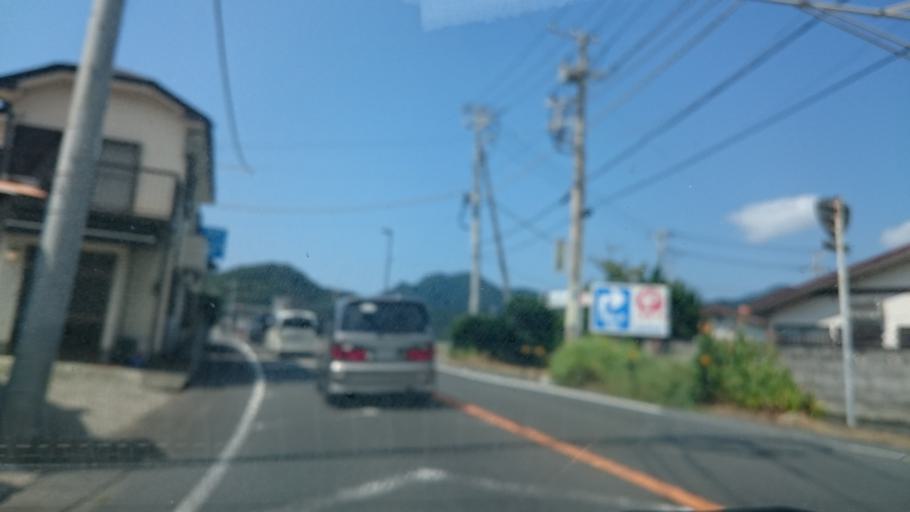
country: JP
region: Shizuoka
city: Heda
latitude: 34.7670
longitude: 138.7783
